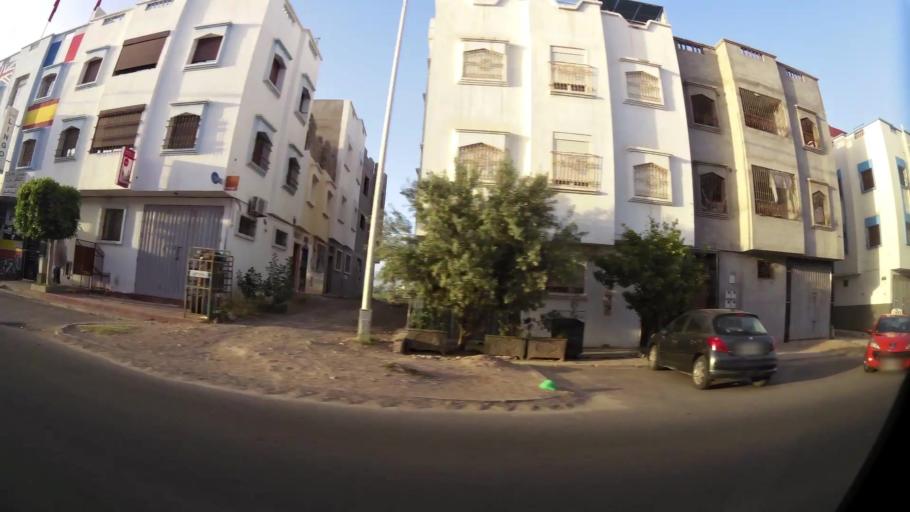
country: MA
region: Oued ed Dahab-Lagouira
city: Dakhla
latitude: 30.3995
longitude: -9.5577
